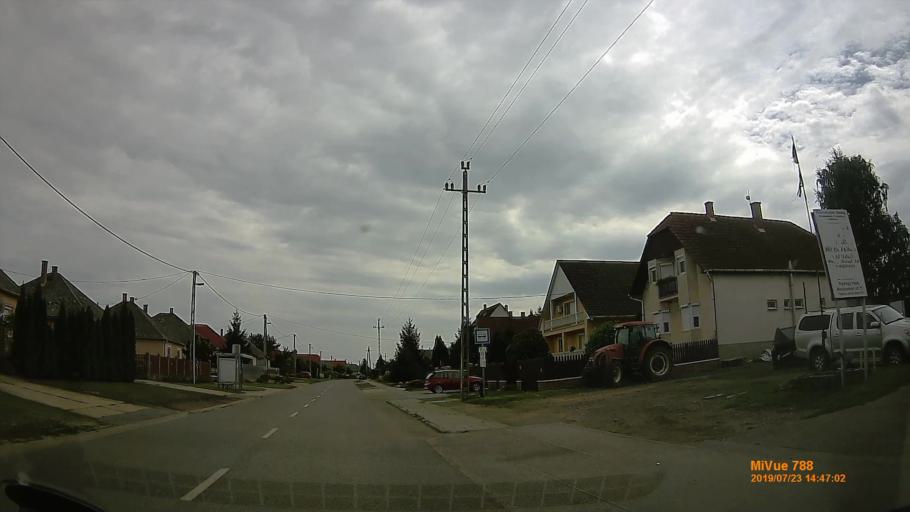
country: HU
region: Szabolcs-Szatmar-Bereg
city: Nyiregyhaza
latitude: 47.9139
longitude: 21.6755
